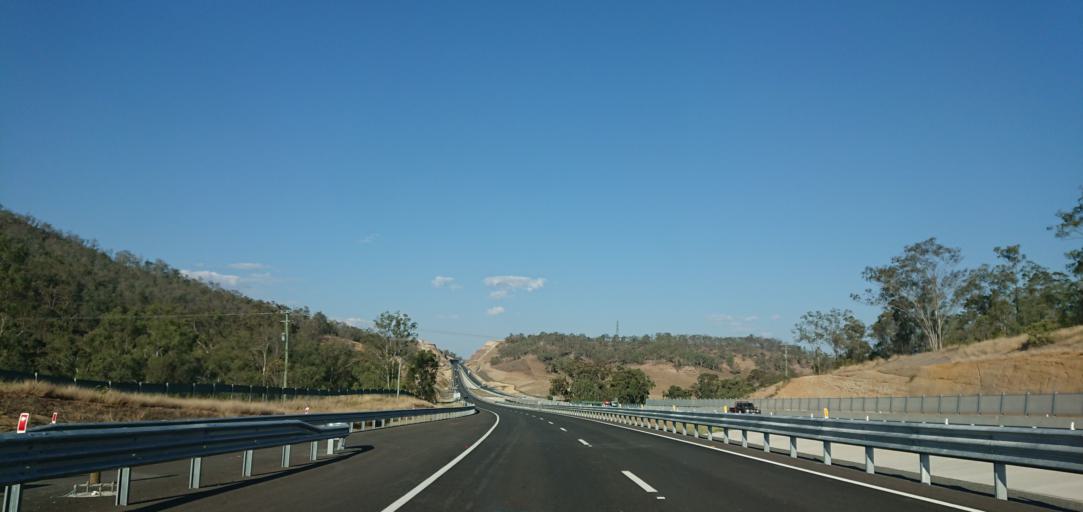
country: AU
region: Queensland
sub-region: Toowoomba
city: East Toowoomba
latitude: -27.5154
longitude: 152.0253
